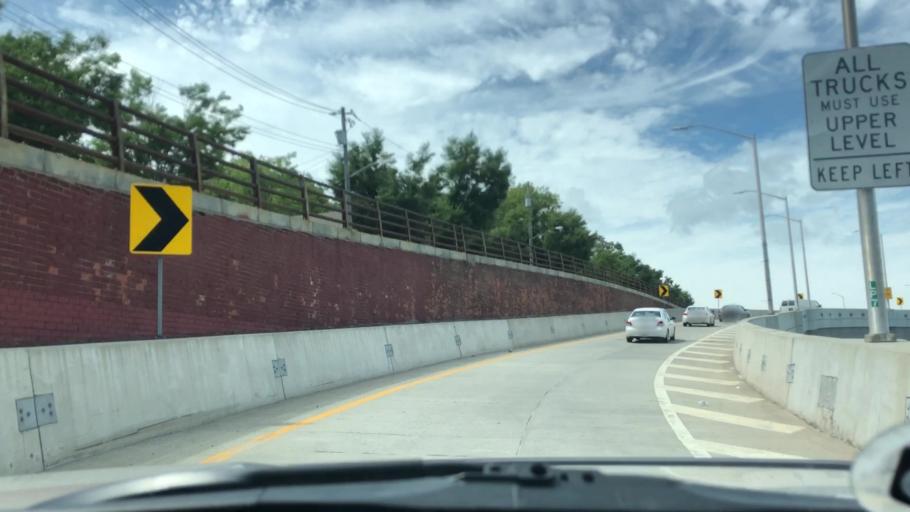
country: US
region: New York
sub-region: Kings County
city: Bensonhurst
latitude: 40.6015
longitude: -74.0661
